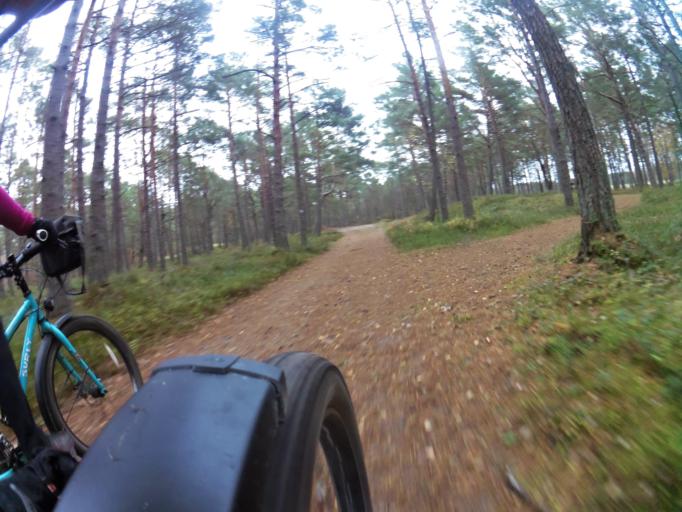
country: PL
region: Pomeranian Voivodeship
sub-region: Powiat leborski
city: Leba
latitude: 54.7783
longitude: 17.7018
